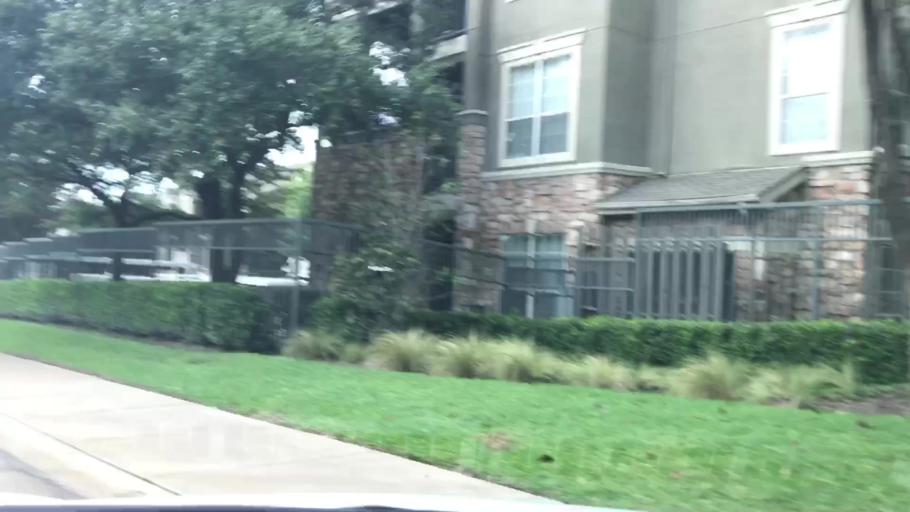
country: US
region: Texas
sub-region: Dallas County
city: Richardson
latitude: 32.9144
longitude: -96.7491
